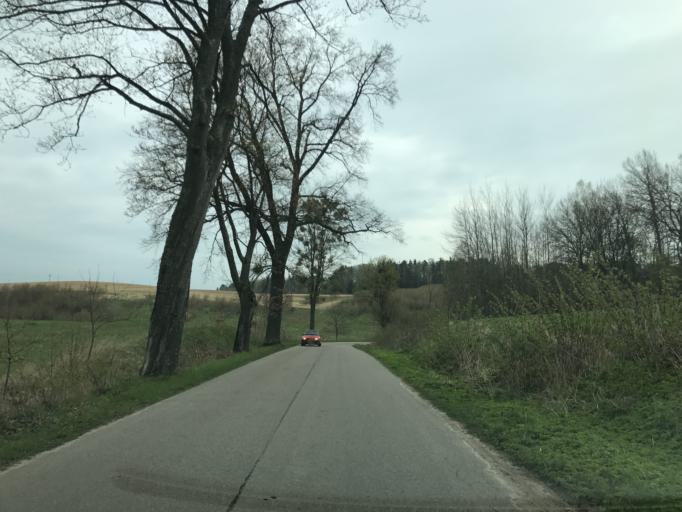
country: PL
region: Warmian-Masurian Voivodeship
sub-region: Powiat ostrodzki
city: Gierzwald
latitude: 53.6372
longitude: 20.0739
